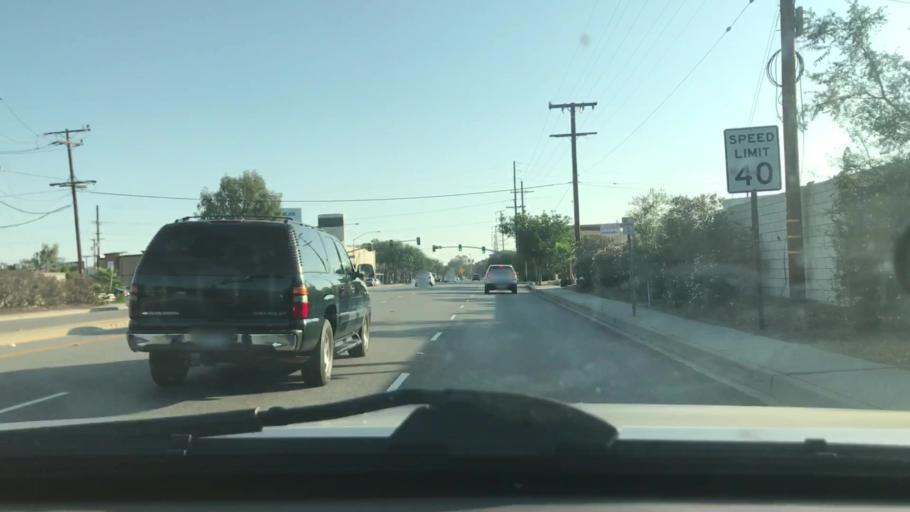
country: US
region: California
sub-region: Los Angeles County
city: Signal Hill
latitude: 33.7975
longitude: -118.1429
